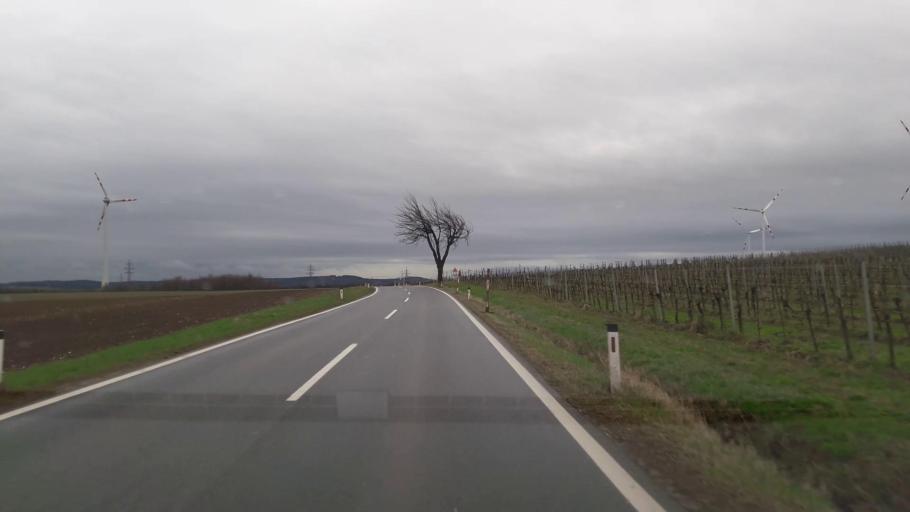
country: AT
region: Lower Austria
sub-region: Politischer Bezirk Bruck an der Leitha
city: Scharndorf
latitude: 48.0598
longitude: 16.7906
